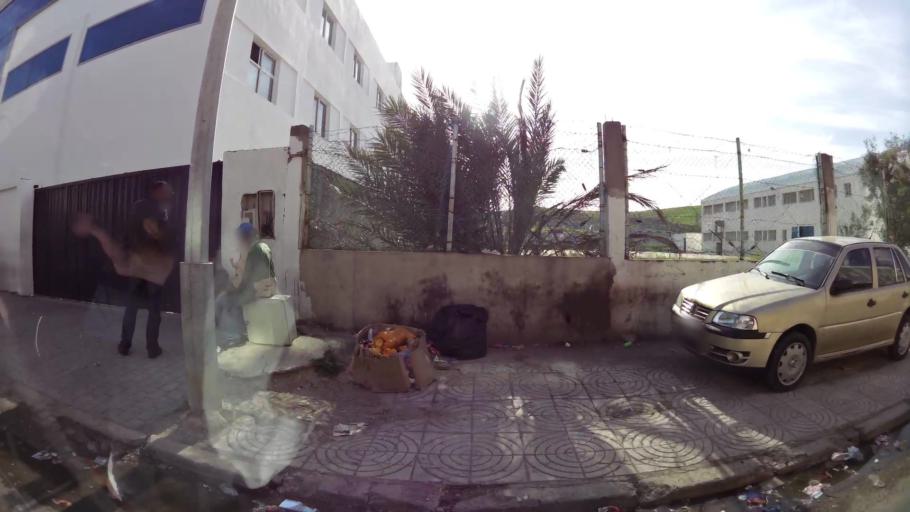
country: MA
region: Tanger-Tetouan
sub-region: Tanger-Assilah
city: Tangier
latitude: 35.7423
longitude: -5.7948
